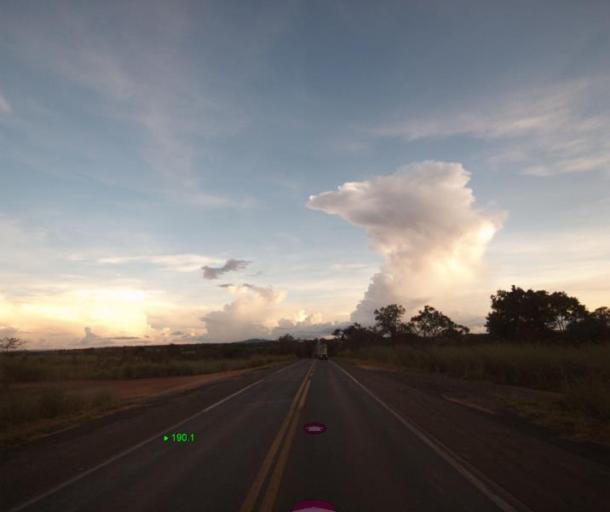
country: BR
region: Goias
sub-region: Uruacu
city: Uruacu
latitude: -14.4401
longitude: -49.1567
